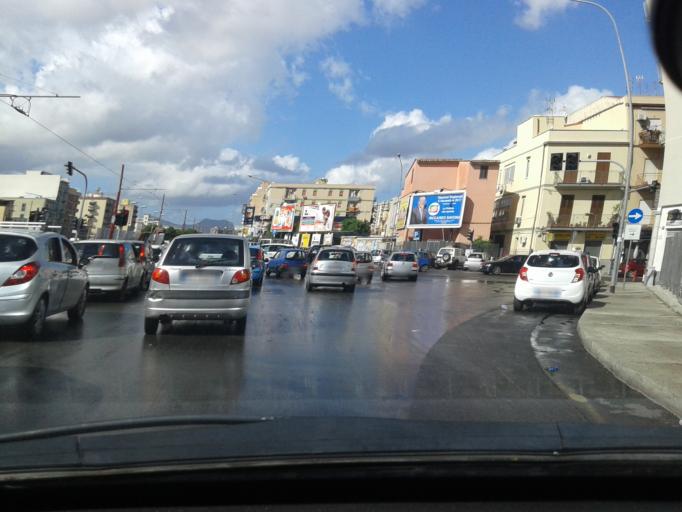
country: IT
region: Sicily
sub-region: Palermo
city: Palermo
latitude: 38.1101
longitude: 13.3302
